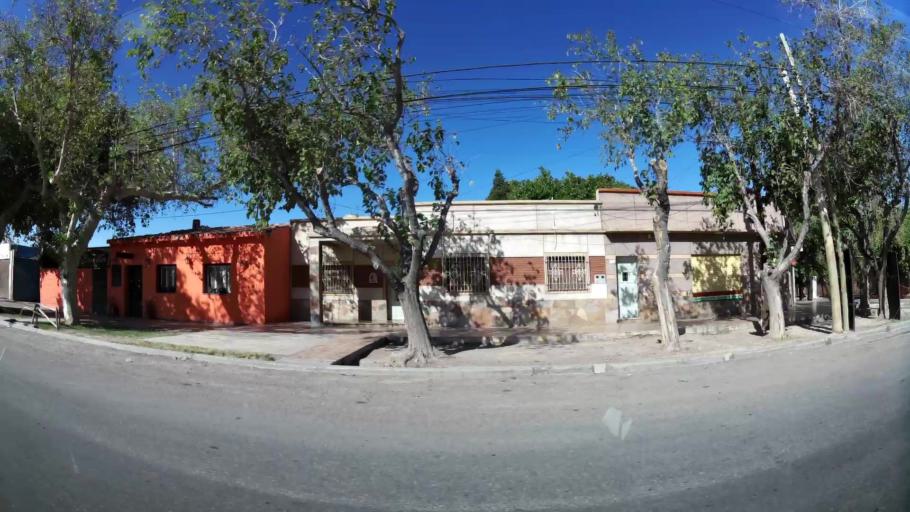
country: AR
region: San Juan
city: Villa Paula de Sarmiento
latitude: -31.5144
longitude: -68.5174
